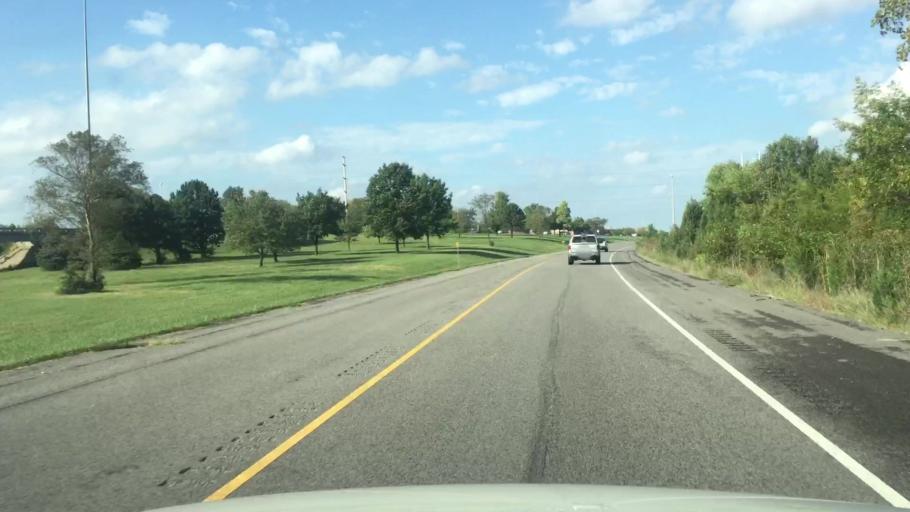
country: US
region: Kansas
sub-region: Johnson County
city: Lenexa
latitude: 38.8996
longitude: -94.6762
